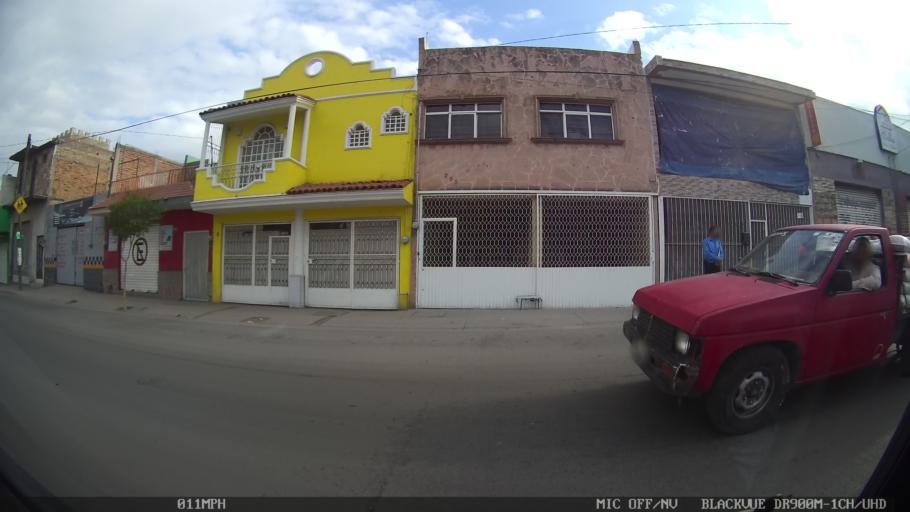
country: MX
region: Jalisco
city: Tlaquepaque
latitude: 20.6770
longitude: -103.2613
